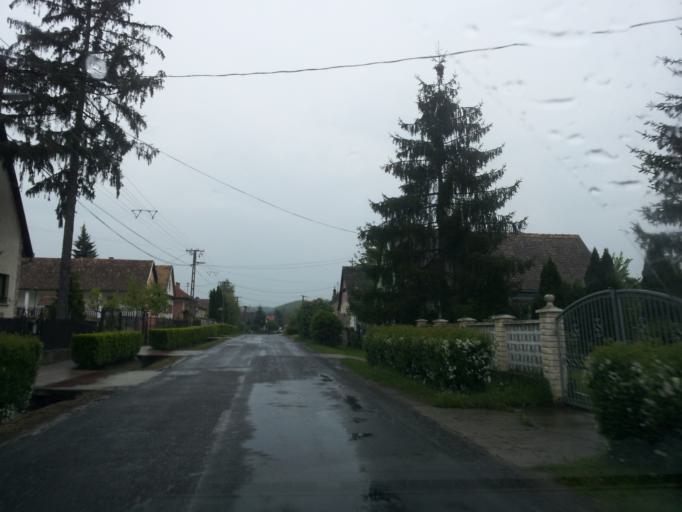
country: HU
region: Tolna
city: Szentgalpuszta
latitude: 46.2791
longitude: 18.6420
